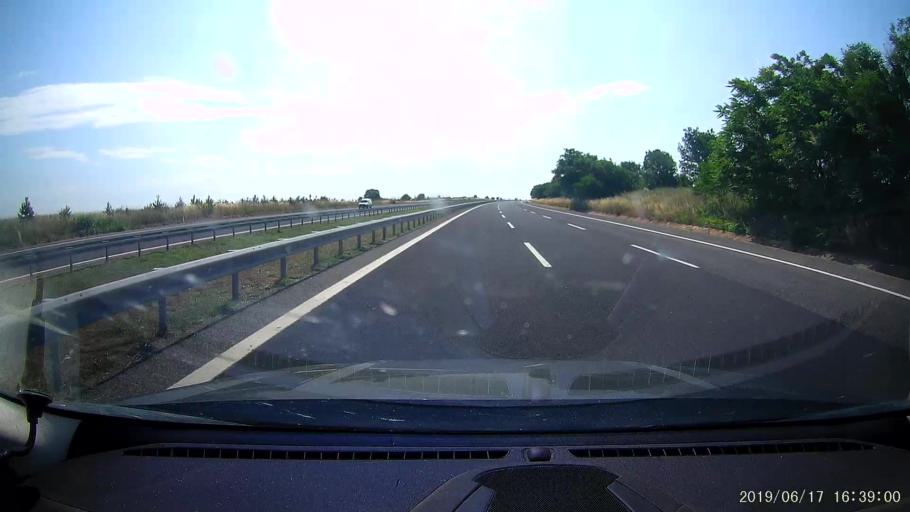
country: TR
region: Kirklareli
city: Luleburgaz
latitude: 41.4468
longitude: 27.4251
